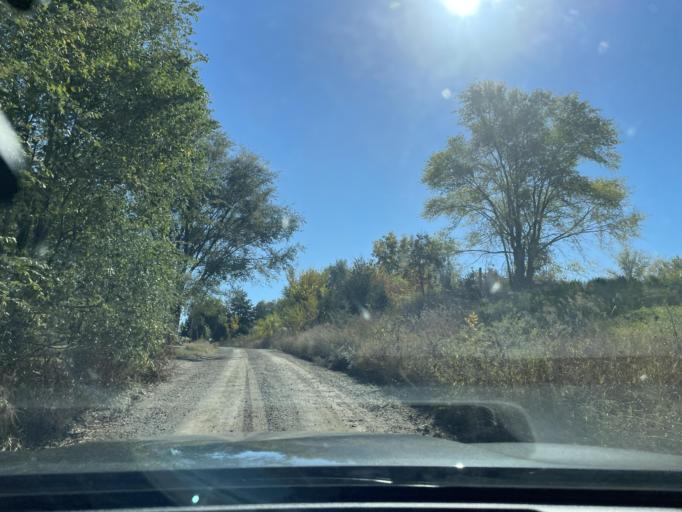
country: US
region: Missouri
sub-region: Andrew County
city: Savannah
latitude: 39.9353
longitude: -94.8627
